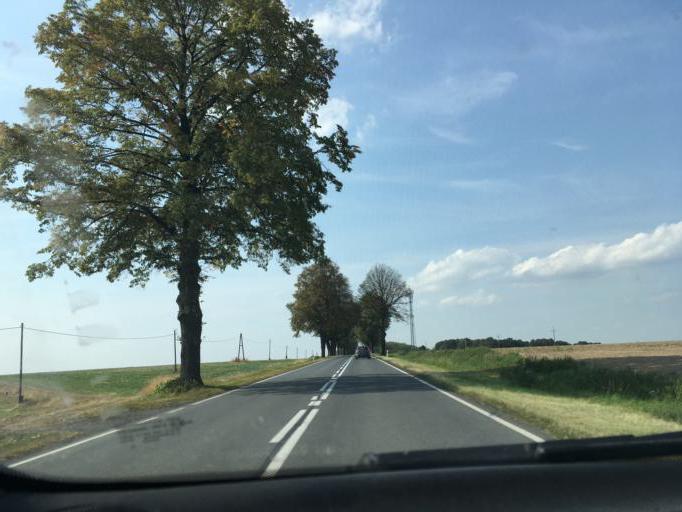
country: PL
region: Opole Voivodeship
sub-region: Powiat prudnicki
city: Laka Prudnicka
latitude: 50.3903
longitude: 17.5163
